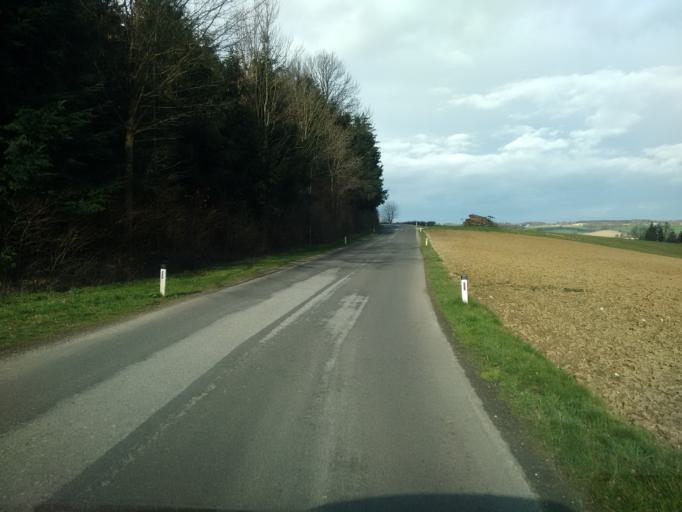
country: AT
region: Upper Austria
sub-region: Politischer Bezirk Linz-Land
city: Ansfelden
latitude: 48.1371
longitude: 14.2491
